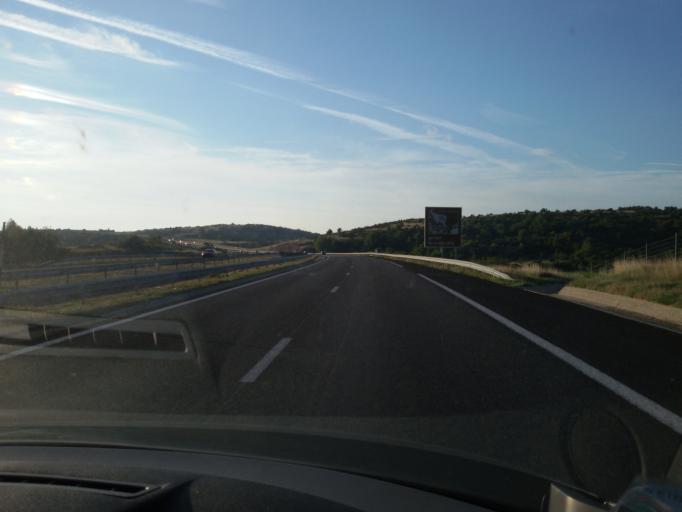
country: FR
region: Midi-Pyrenees
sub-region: Departement de l'Aveyron
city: La Cavalerie
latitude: 43.9020
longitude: 3.2779
